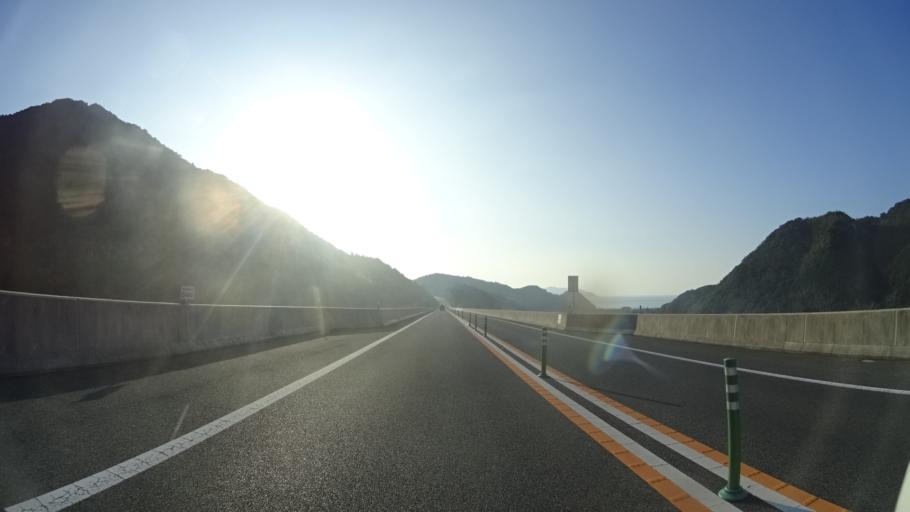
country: JP
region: Yamaguchi
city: Hagi
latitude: 34.3871
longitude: 131.3420
